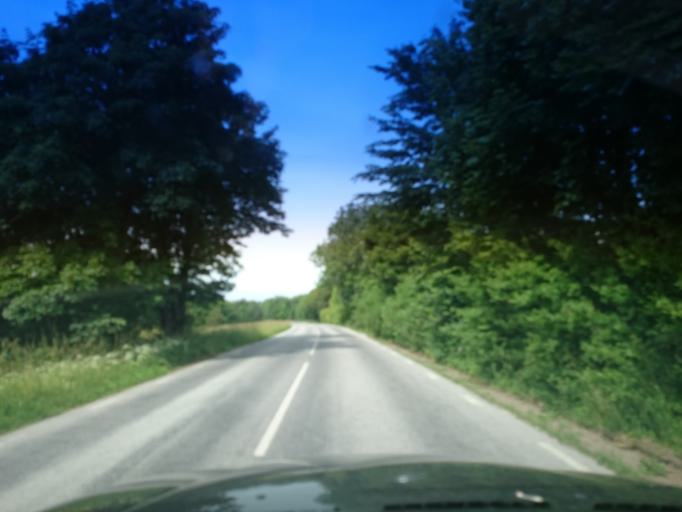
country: SE
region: Gotland
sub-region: Gotland
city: Hemse
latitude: 57.2482
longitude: 18.5005
